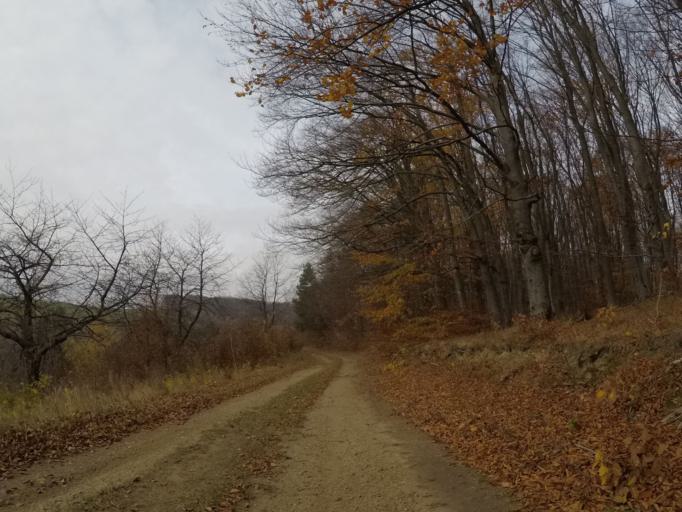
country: SK
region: Presovsky
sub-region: Okres Presov
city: Presov
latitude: 48.9284
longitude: 21.1390
